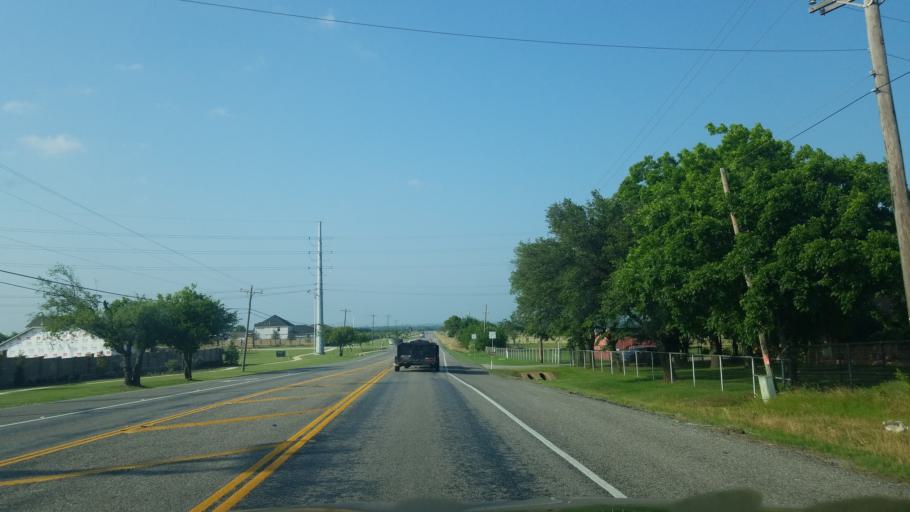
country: US
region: Texas
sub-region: Denton County
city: Denton
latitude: 33.2631
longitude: -97.1061
